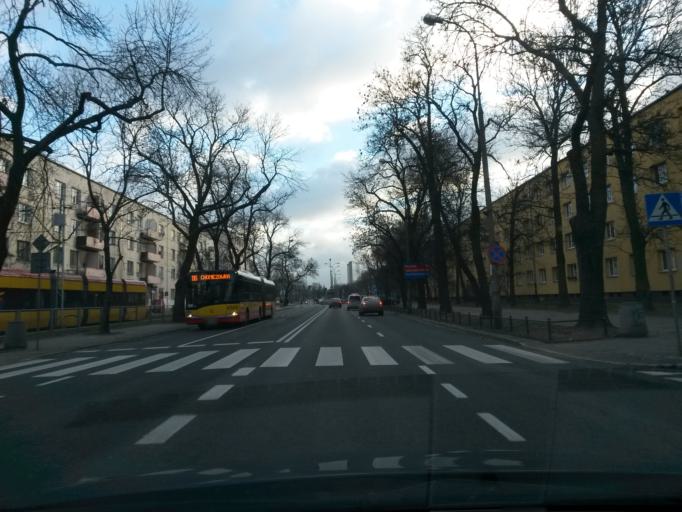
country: PL
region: Masovian Voivodeship
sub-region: Warszawa
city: Zoliborz
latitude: 52.2664
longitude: 20.9886
